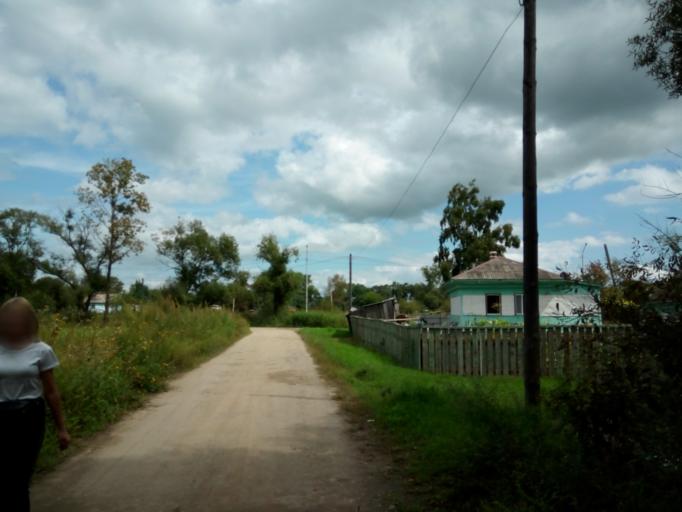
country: RU
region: Primorskiy
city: Dal'nerechensk
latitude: 45.9359
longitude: 133.8107
